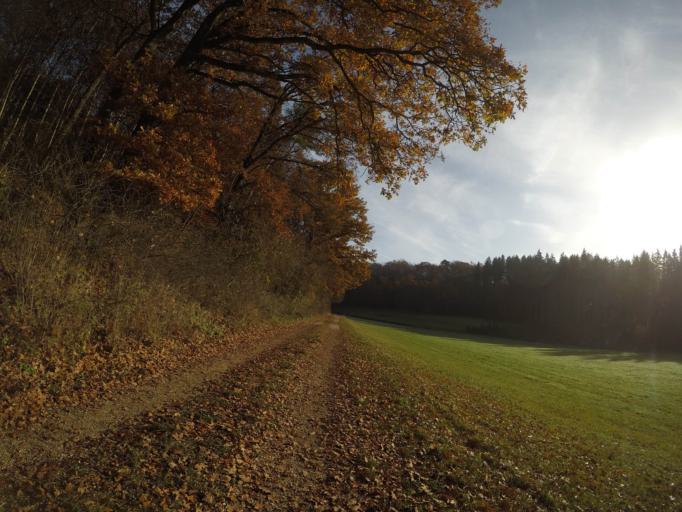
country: DE
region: Baden-Wuerttemberg
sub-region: Tuebingen Region
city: Bernstadt
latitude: 48.5159
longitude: 10.0253
